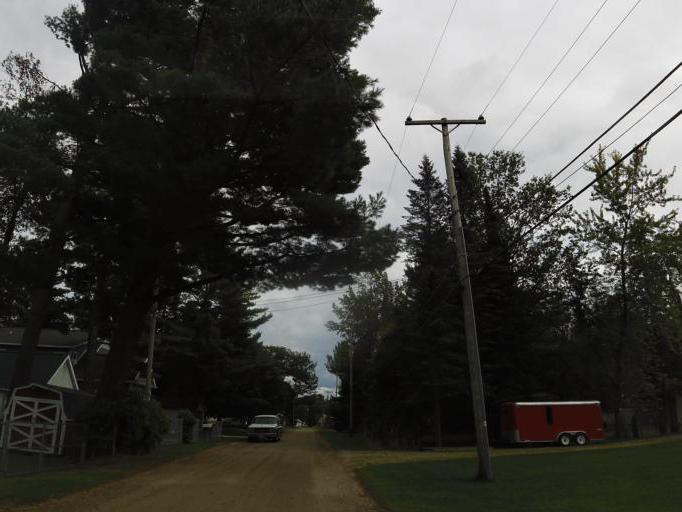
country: US
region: Michigan
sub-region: Roscommon County
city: Saint Helen
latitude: 44.3556
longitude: -84.4881
